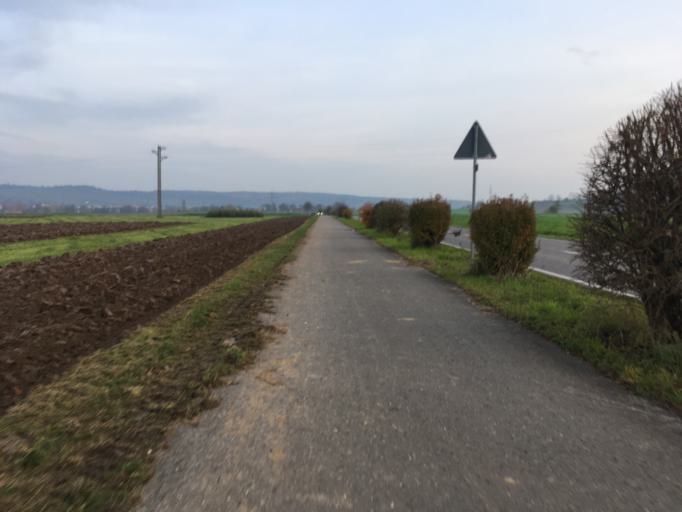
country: DE
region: Baden-Wuerttemberg
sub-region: Karlsruhe Region
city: Hassmersheim
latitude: 49.2836
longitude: 9.1418
